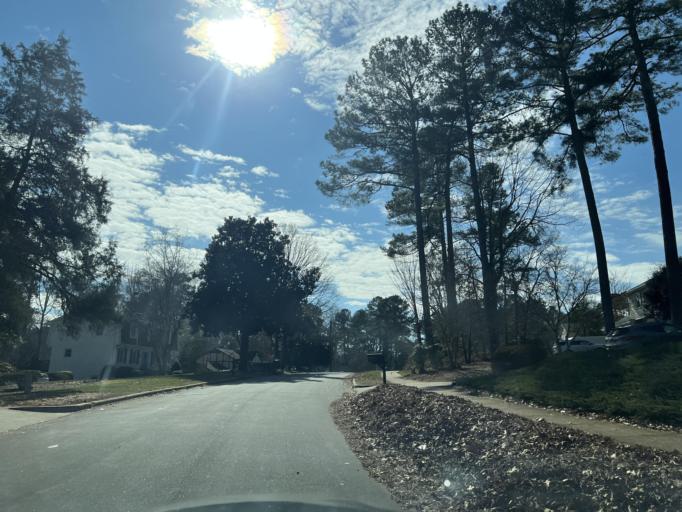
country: US
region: North Carolina
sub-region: Wake County
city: West Raleigh
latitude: 35.8803
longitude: -78.6209
